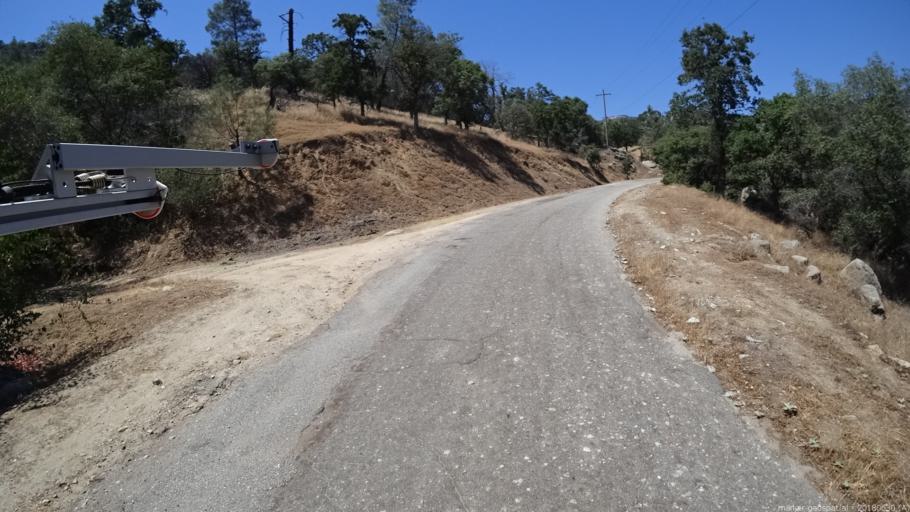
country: US
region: California
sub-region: Fresno County
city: Auberry
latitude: 37.1550
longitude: -119.4377
